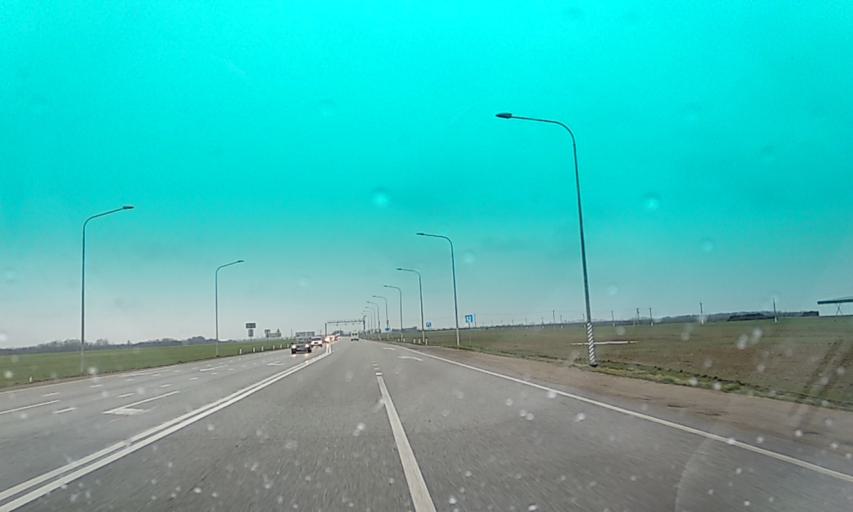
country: RU
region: Krasnodarskiy
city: Belorechensk
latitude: 44.8285
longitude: 39.8440
